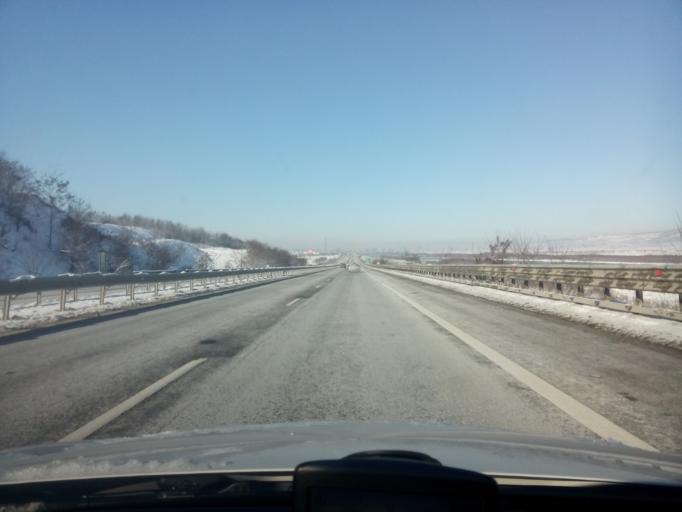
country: RO
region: Arges
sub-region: Oras Stefanesti
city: Golesti
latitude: 44.8191
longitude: 24.9462
